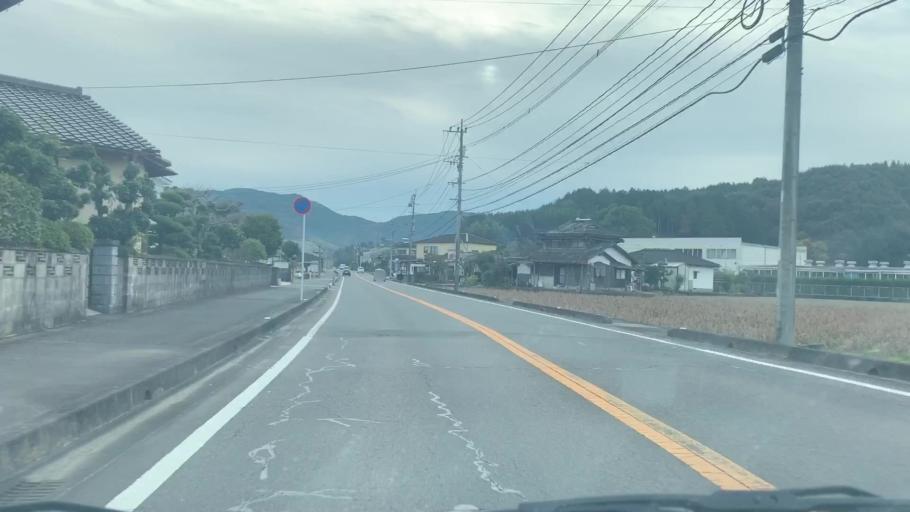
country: JP
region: Saga Prefecture
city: Takeocho-takeo
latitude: 33.1685
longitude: 130.0512
